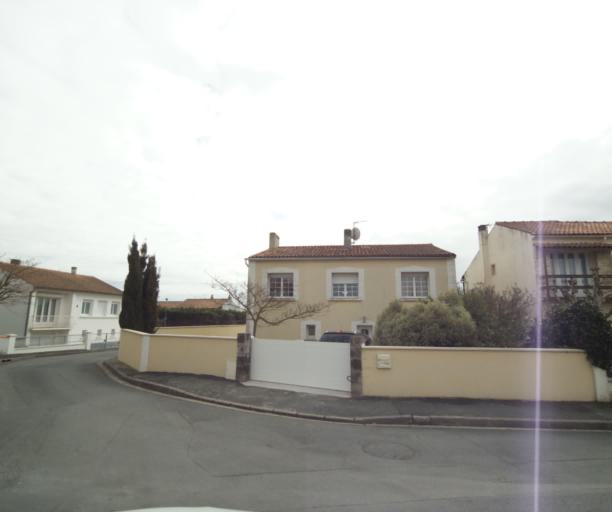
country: FR
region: Poitou-Charentes
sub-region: Departement de la Charente-Maritime
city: Lagord
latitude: 46.1894
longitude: -1.1515
